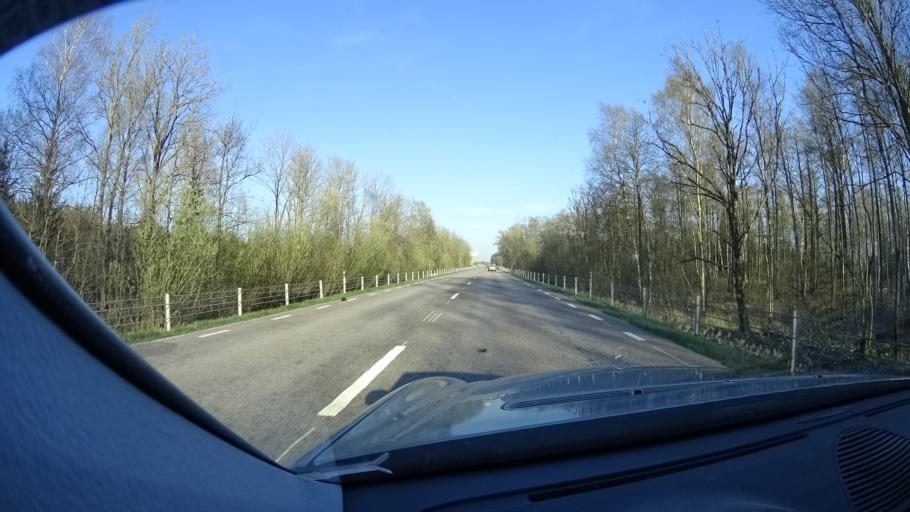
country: SE
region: Skane
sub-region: Eslovs Kommun
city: Stehag
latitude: 55.8528
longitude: 13.3972
